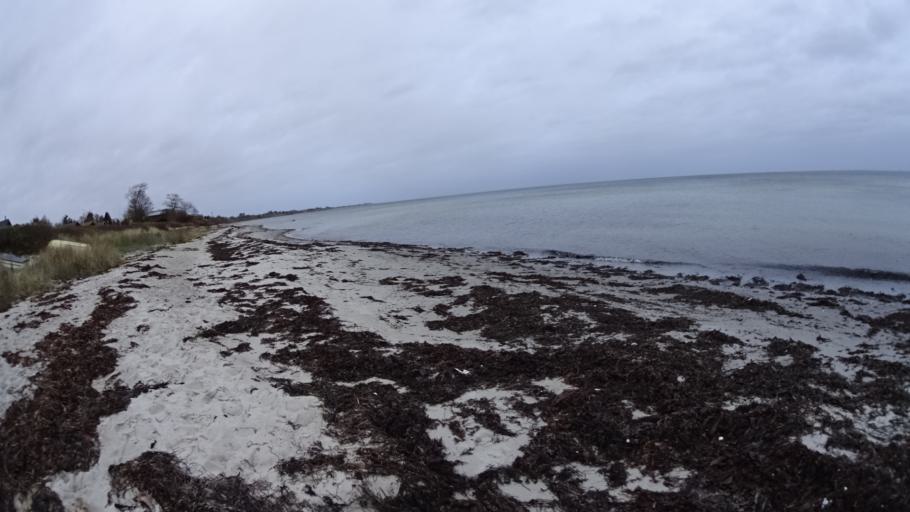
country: DK
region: Central Jutland
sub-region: Arhus Kommune
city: Malling
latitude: 55.9832
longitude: 10.2523
